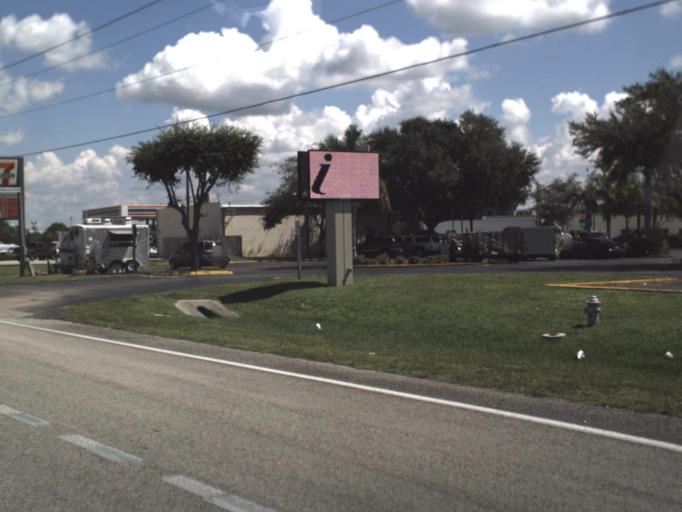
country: US
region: Florida
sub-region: Lee County
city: Lochmoor Waterway Estates
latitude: 26.6668
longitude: -81.9425
